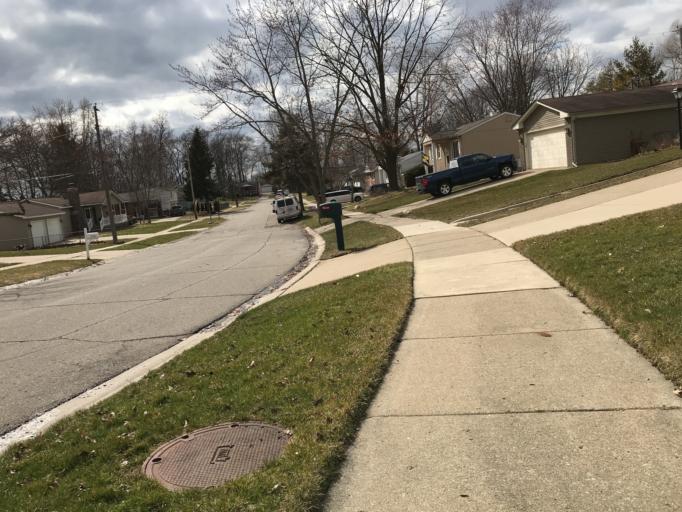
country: US
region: Michigan
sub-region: Oakland County
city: South Lyon
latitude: 42.4678
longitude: -83.6415
